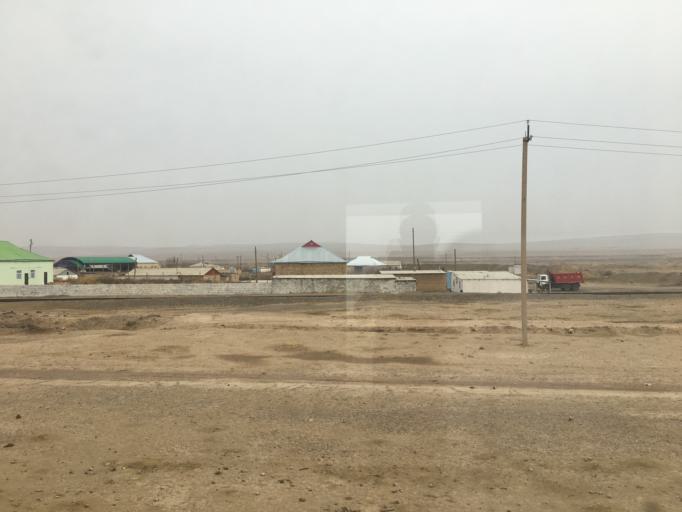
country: TM
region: Mary
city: Serhetabat
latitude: 35.6476
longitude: 62.5542
